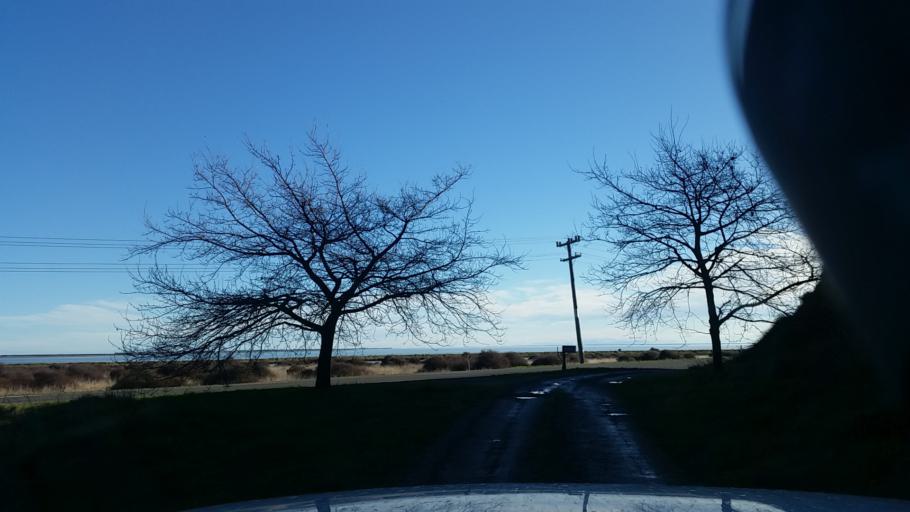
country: NZ
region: Canterbury
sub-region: Selwyn District
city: Lincoln
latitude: -43.7864
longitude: 172.6617
